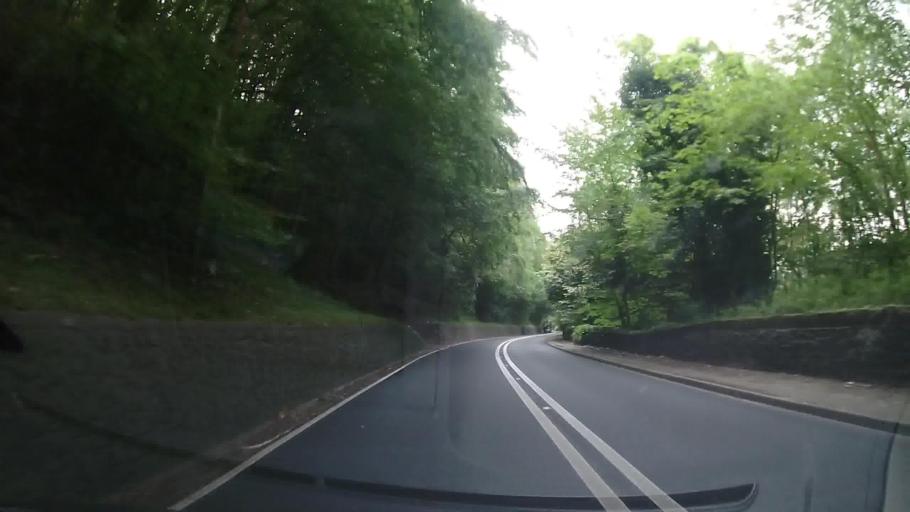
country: GB
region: Wales
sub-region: Denbighshire
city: Llangollen
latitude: 52.9627
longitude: -3.1246
